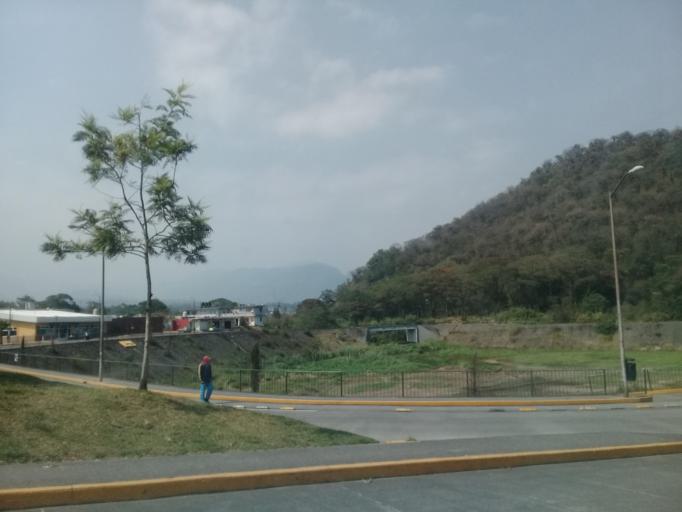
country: MX
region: Veracruz
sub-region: Mariano Escobedo
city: Palmira
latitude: 18.8789
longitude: -97.1039
